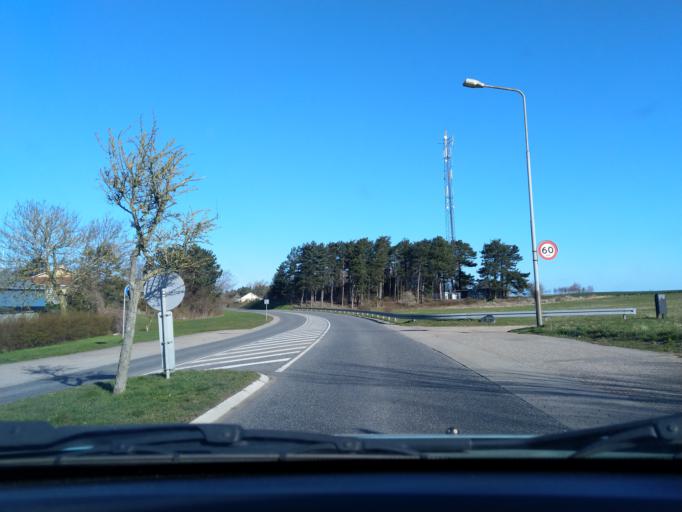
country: DK
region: Zealand
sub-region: Kalundborg Kommune
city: Kalundborg
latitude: 55.7111
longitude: 11.0208
